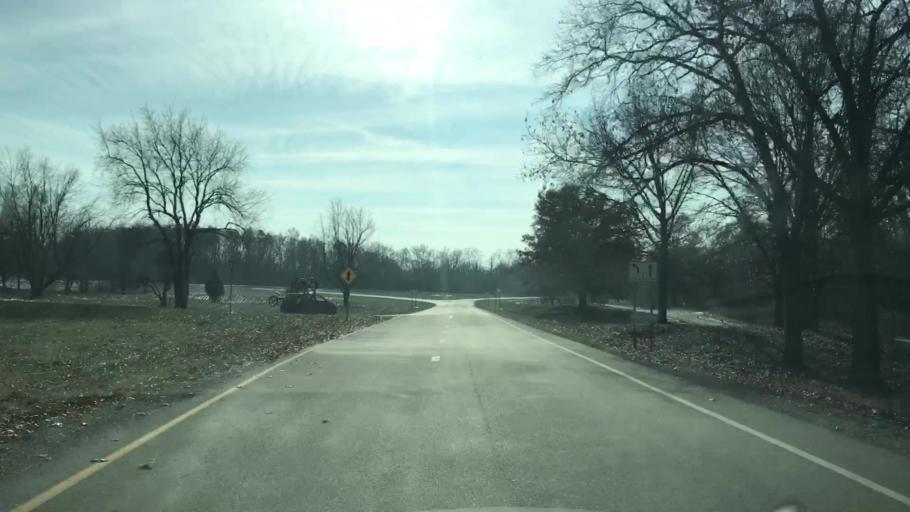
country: US
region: Michigan
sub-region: Macomb County
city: Shelby
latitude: 42.7245
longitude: -83.0739
